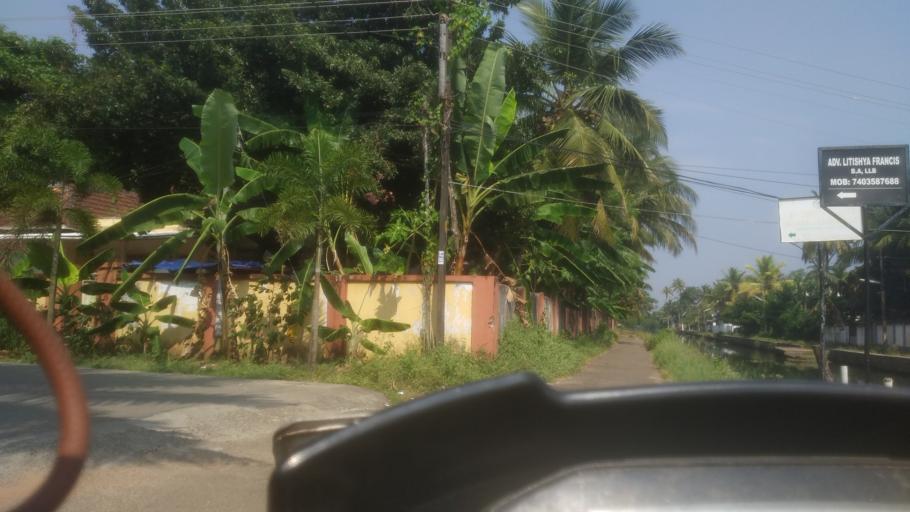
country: IN
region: Kerala
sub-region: Ernakulam
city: Elur
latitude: 10.0493
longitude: 76.2208
